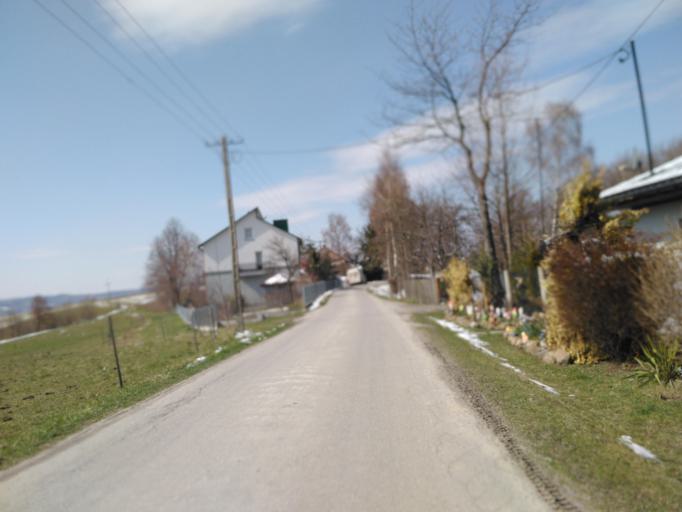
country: PL
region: Subcarpathian Voivodeship
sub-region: Powiat ropczycko-sedziszowski
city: Niedzwiada
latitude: 49.9973
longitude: 21.5773
